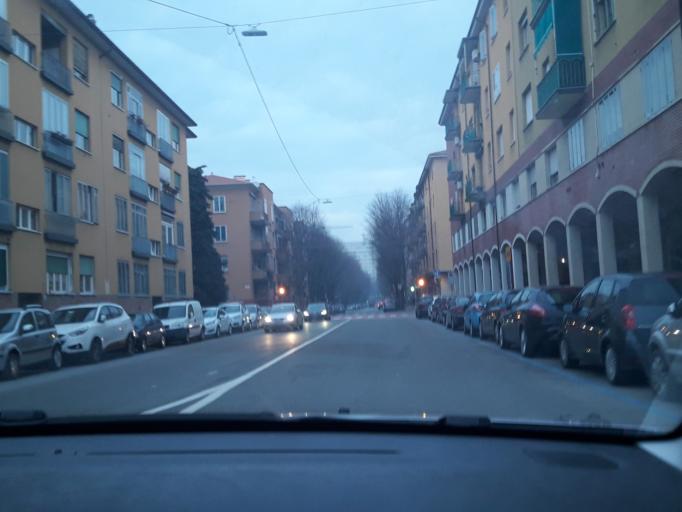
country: IT
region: Emilia-Romagna
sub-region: Provincia di Bologna
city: Bologna
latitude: 44.5000
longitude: 11.3106
